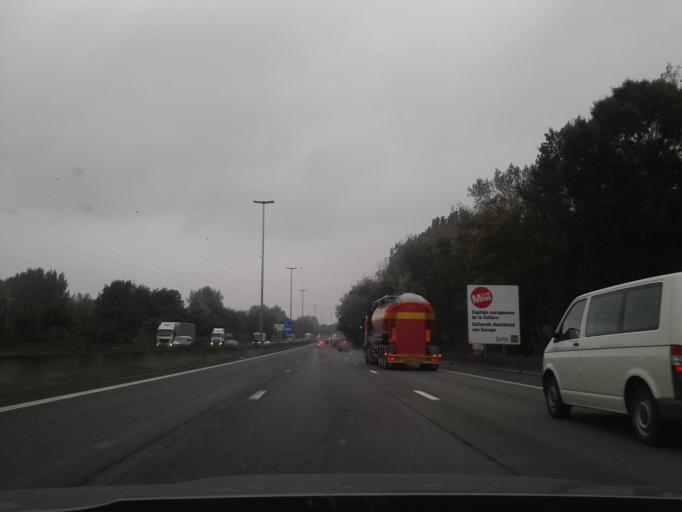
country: BE
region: Wallonia
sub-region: Province du Hainaut
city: Mons
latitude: 50.4726
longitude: 3.9354
